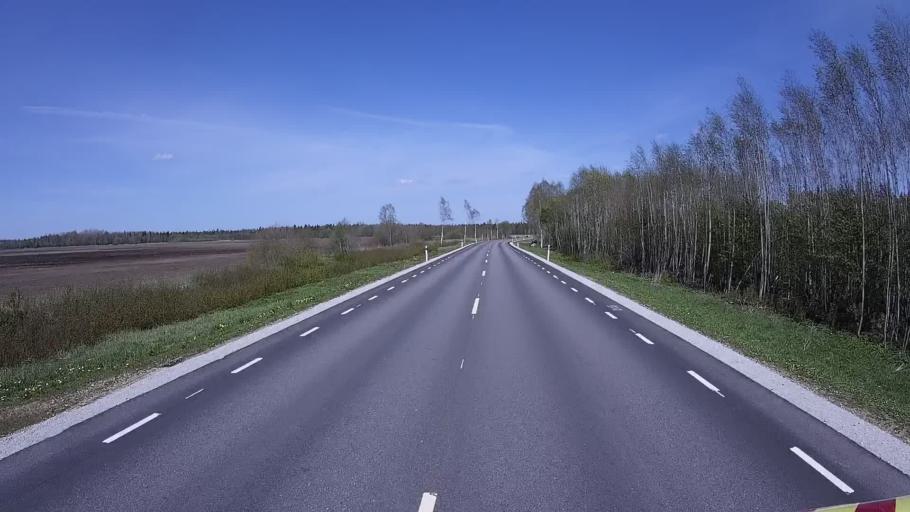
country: EE
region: Harju
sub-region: Nissi vald
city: Turba
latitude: 59.1683
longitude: 24.0743
